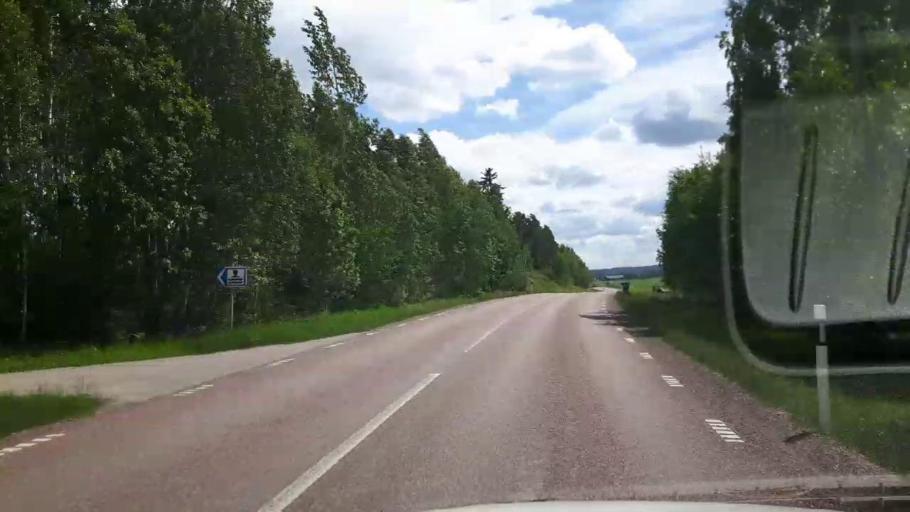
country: SE
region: Dalarna
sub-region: Saters Kommun
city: Saeter
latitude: 60.4108
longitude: 15.8579
